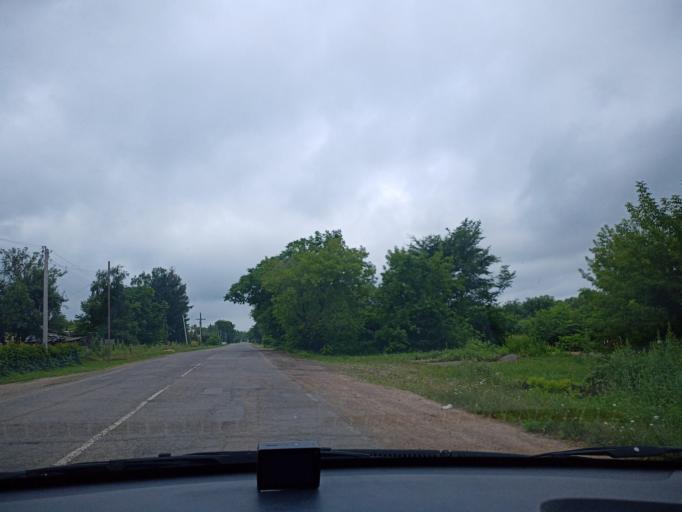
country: RU
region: Primorskiy
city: Novopokrovka
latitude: 45.8938
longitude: 134.8608
